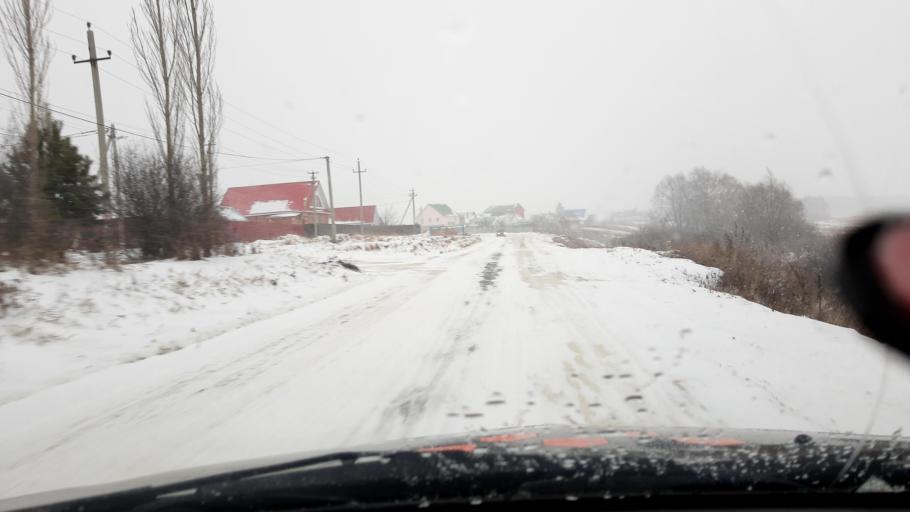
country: RU
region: Bashkortostan
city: Ufa
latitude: 54.5471
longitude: 55.9452
